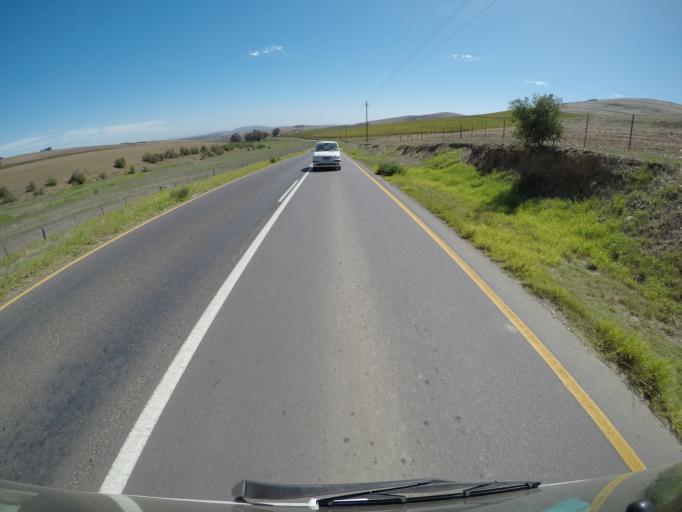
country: ZA
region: Western Cape
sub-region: City of Cape Town
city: Sunset Beach
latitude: -33.7910
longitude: 18.6008
